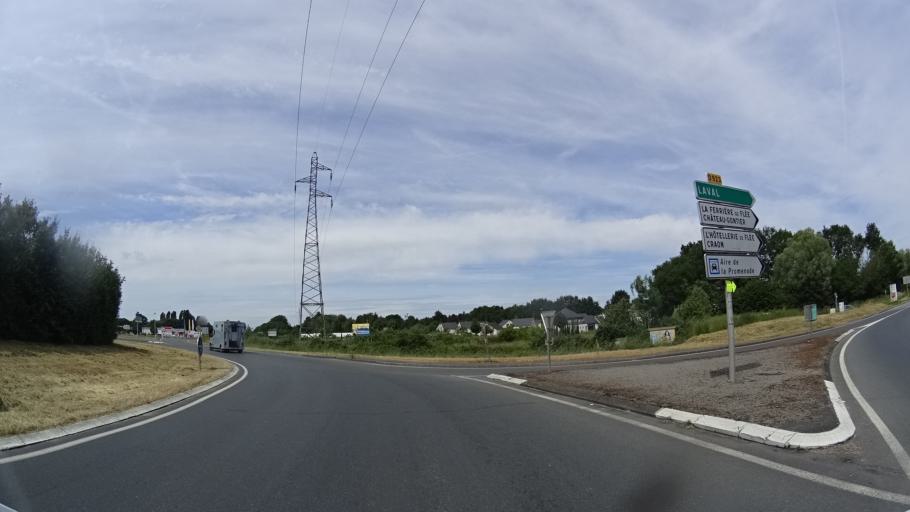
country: FR
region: Pays de la Loire
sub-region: Departement de Maine-et-Loire
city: Segre
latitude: 47.6974
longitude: -0.8692
